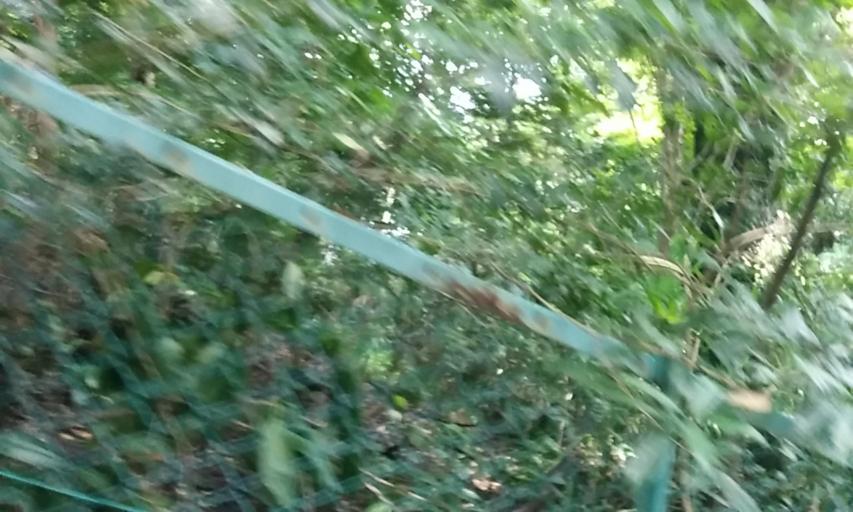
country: JP
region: Tokyo
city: Kokubunji
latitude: 35.6939
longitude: 139.4712
